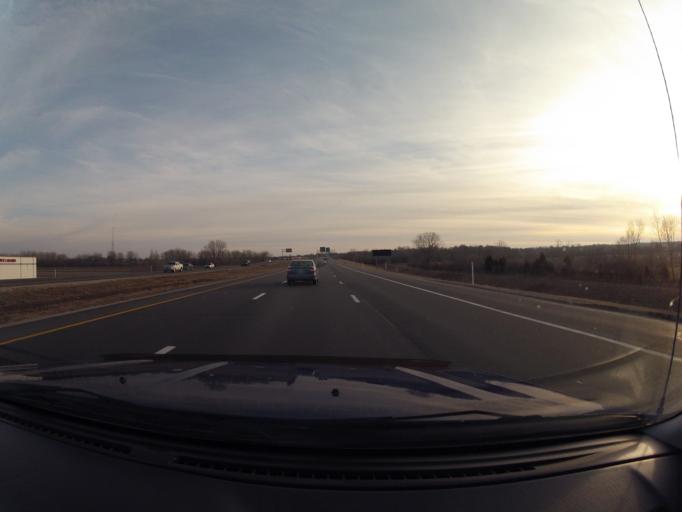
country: US
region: Kansas
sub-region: Shawnee County
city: Topeka
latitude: 39.0771
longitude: -95.7310
